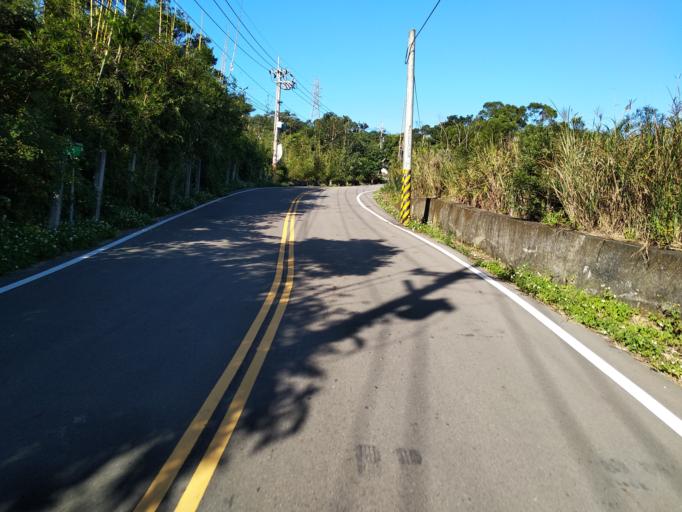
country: TW
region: Taiwan
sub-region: Hsinchu
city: Zhubei
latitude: 24.8661
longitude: 121.0966
